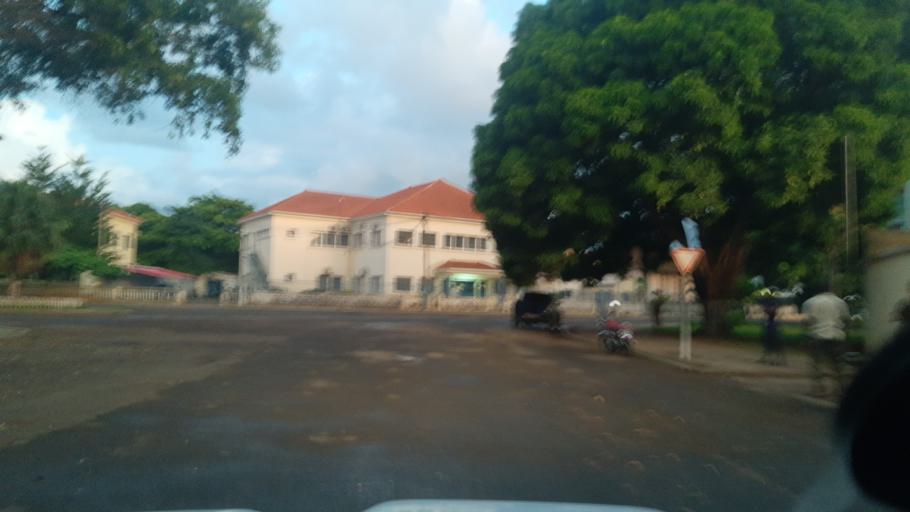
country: ST
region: Sao Tome Island
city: Sao Tome
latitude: 0.3450
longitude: 6.7369
